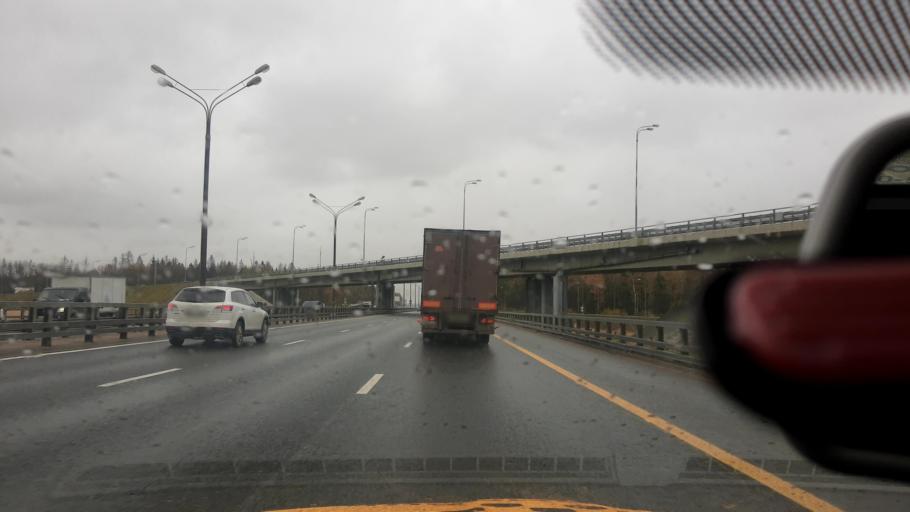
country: RU
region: Moskovskaya
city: Kokoshkino
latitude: 55.6248
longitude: 37.1741
